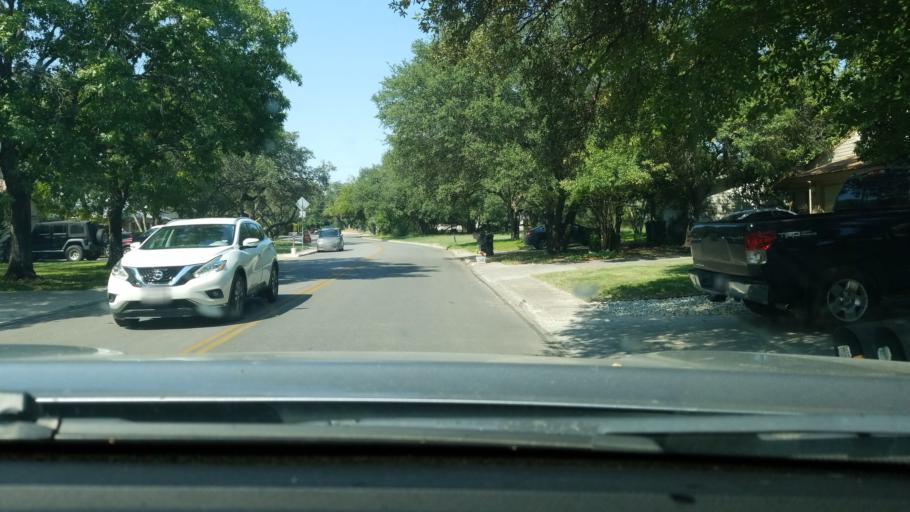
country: US
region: Texas
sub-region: Bexar County
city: Shavano Park
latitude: 29.5614
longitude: -98.6059
